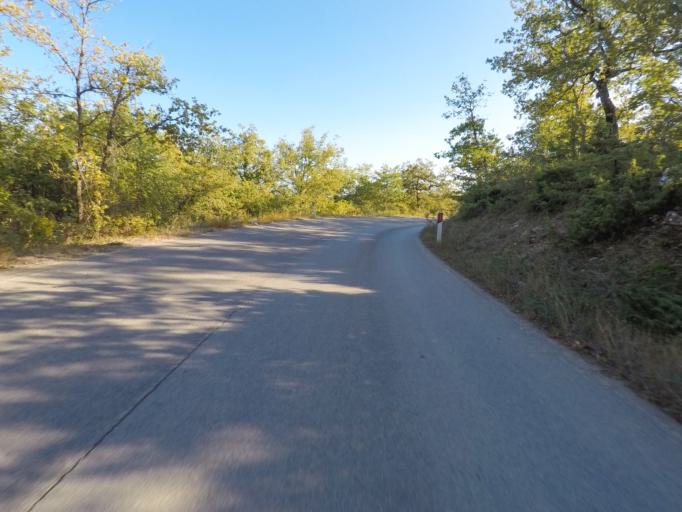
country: IT
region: Tuscany
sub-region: Provincia di Siena
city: Gaiole in Chianti
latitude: 43.4455
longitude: 11.3947
